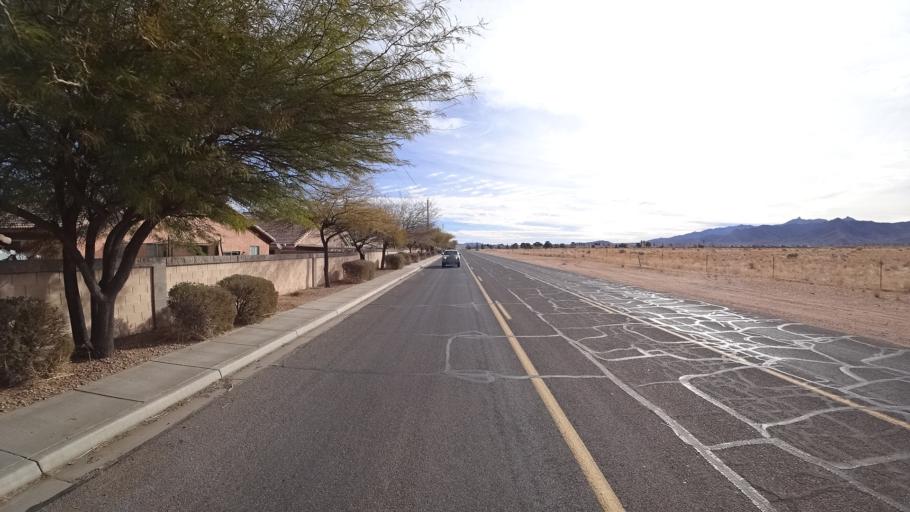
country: US
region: Arizona
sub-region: Mohave County
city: New Kingman-Butler
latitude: 35.2250
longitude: -113.9819
